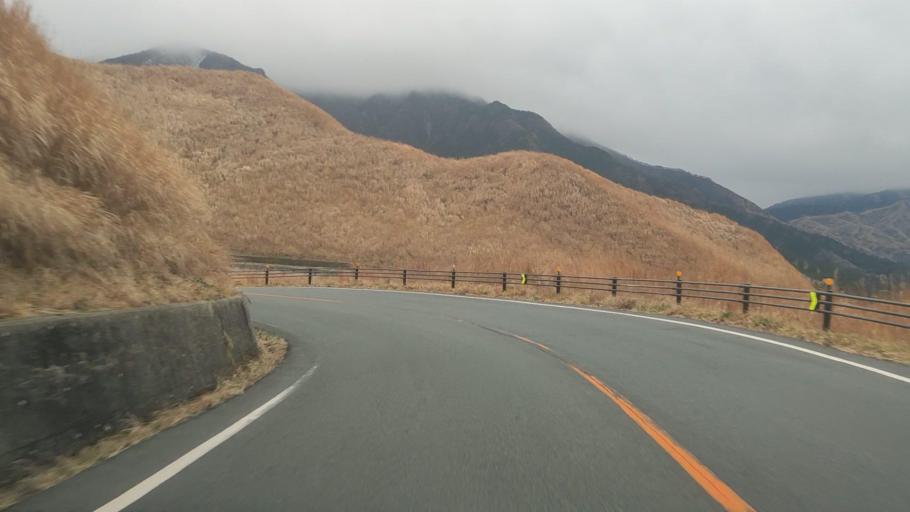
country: JP
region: Kumamoto
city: Aso
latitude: 32.9061
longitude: 131.1541
